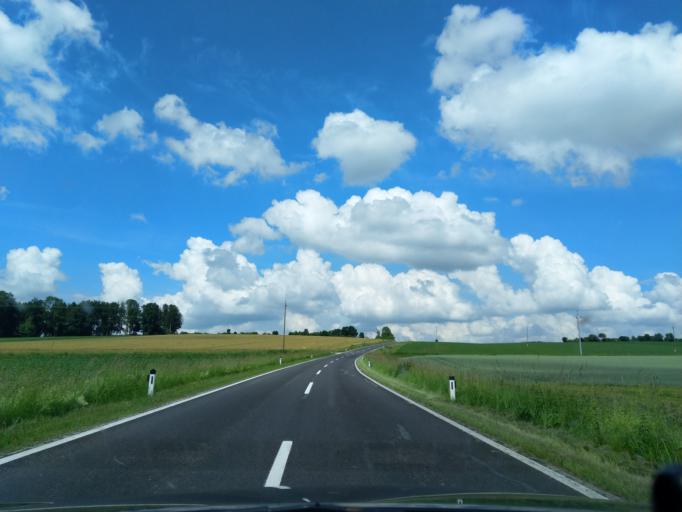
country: DE
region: Bavaria
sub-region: Lower Bavaria
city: Bad Fussing
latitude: 48.2619
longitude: 13.3704
